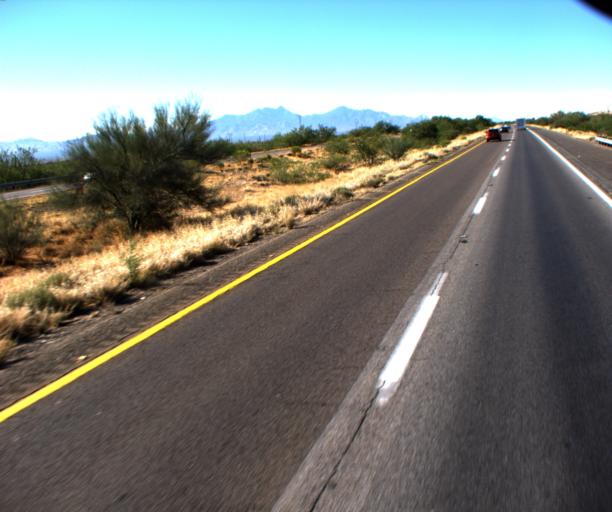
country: US
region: Arizona
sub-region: Pima County
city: Sahuarita
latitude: 31.9950
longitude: -110.9923
